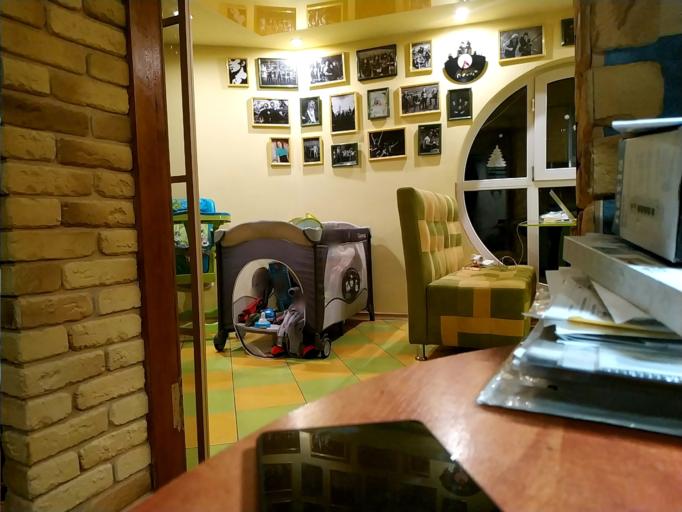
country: RU
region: Orjol
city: Naryshkino
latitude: 53.0115
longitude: 35.6929
